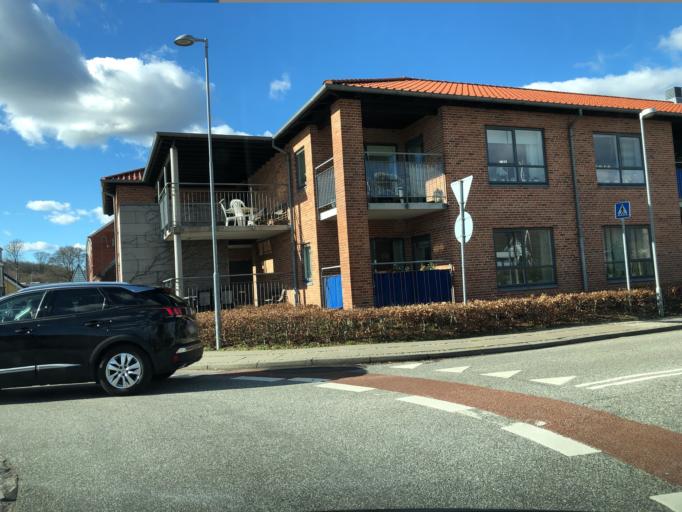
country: DK
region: Central Jutland
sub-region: Favrskov Kommune
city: Hinnerup
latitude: 56.2631
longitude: 10.0635
